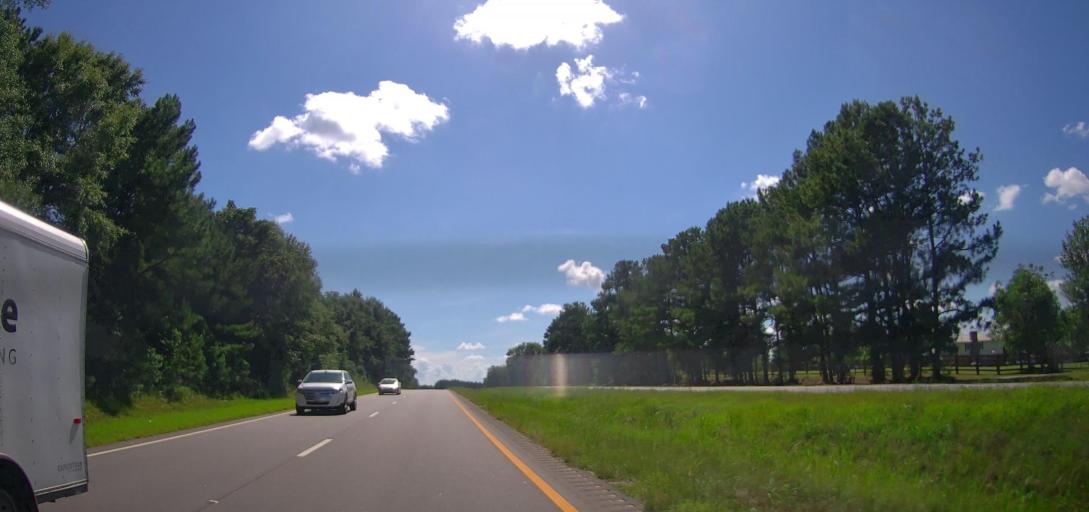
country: US
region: Alabama
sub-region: Macon County
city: Tuskegee
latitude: 32.3806
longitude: -85.7725
